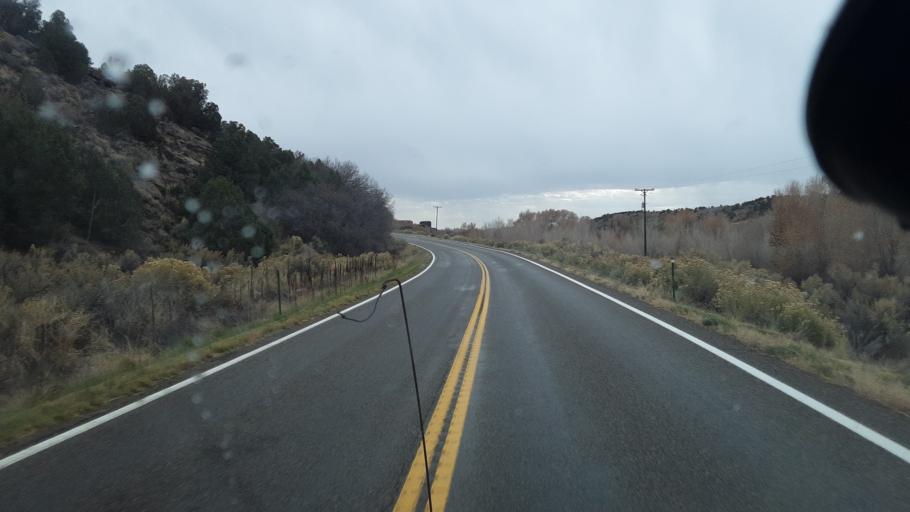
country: US
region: New Mexico
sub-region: San Juan County
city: Spencerville
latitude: 37.0455
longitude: -108.1824
